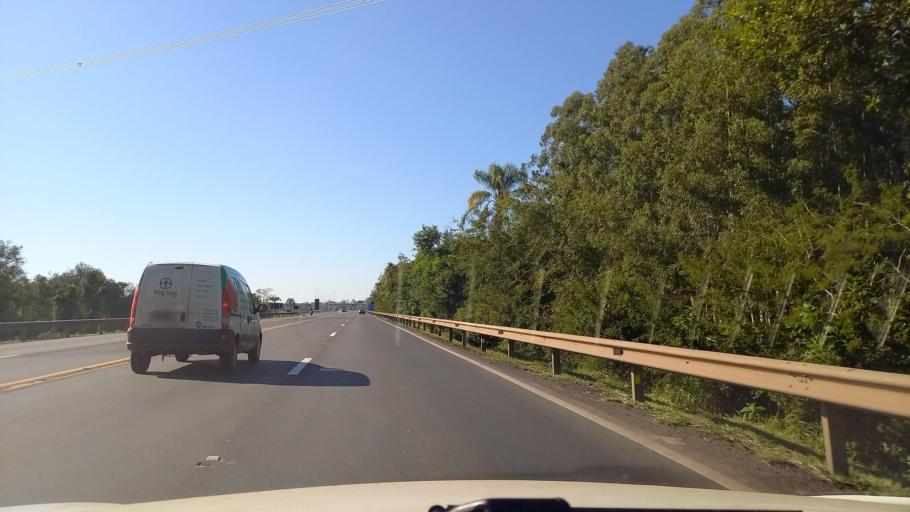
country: BR
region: Rio Grande do Sul
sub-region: Montenegro
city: Montenegro
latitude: -29.8188
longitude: -51.3691
